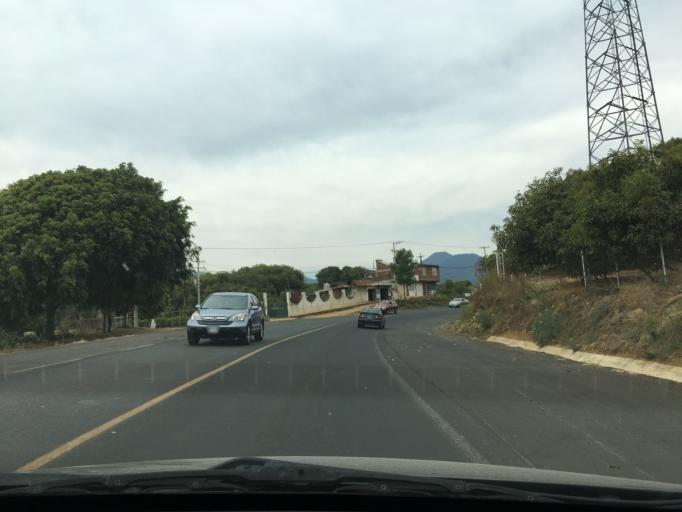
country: MX
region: Michoacan
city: Nuevo San Juan Parangaricutiro
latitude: 19.4068
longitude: -102.1141
